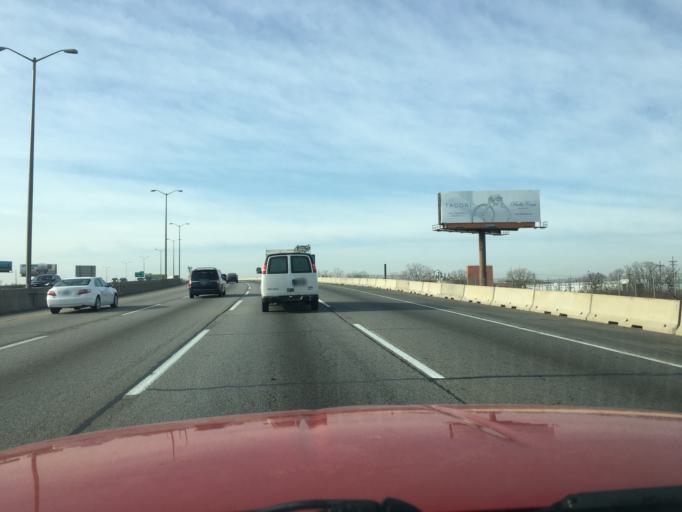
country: US
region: Illinois
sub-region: Cook County
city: Northlake
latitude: 41.9386
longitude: -87.9113
